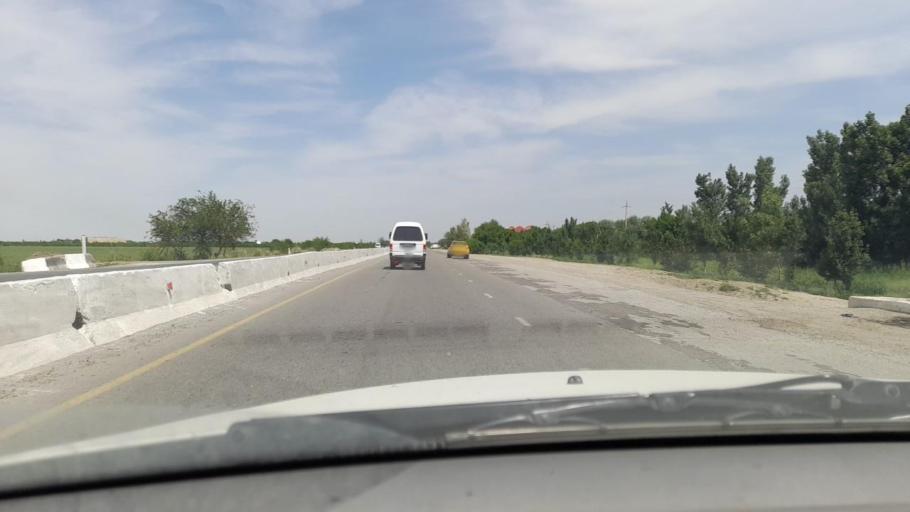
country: UZ
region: Bukhara
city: Wobkent
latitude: 40.0408
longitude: 64.5378
